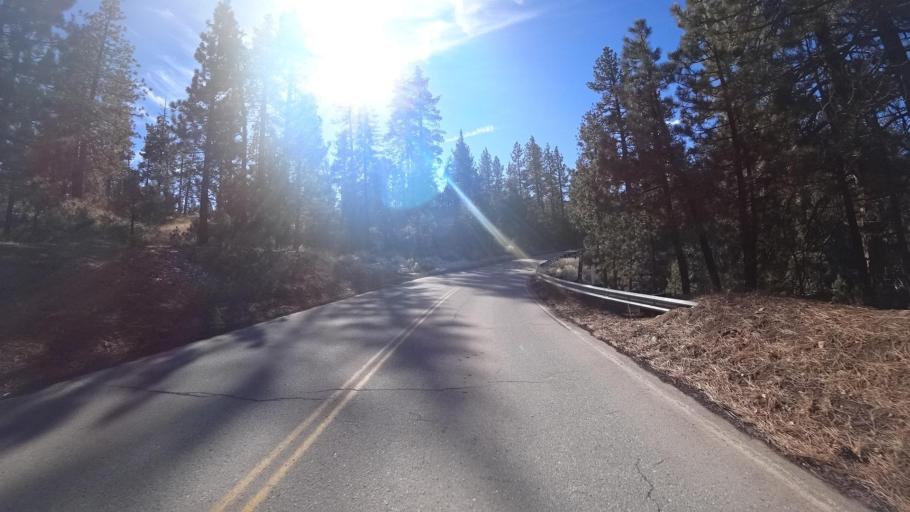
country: US
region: California
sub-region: Kern County
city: Pine Mountain Club
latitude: 34.8450
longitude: -119.0844
